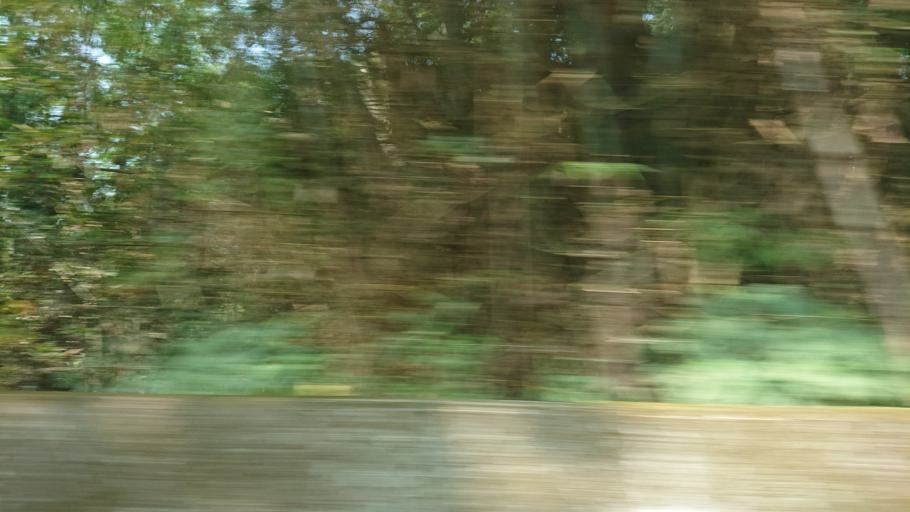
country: TW
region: Taiwan
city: Lugu
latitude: 23.6974
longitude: 120.6629
